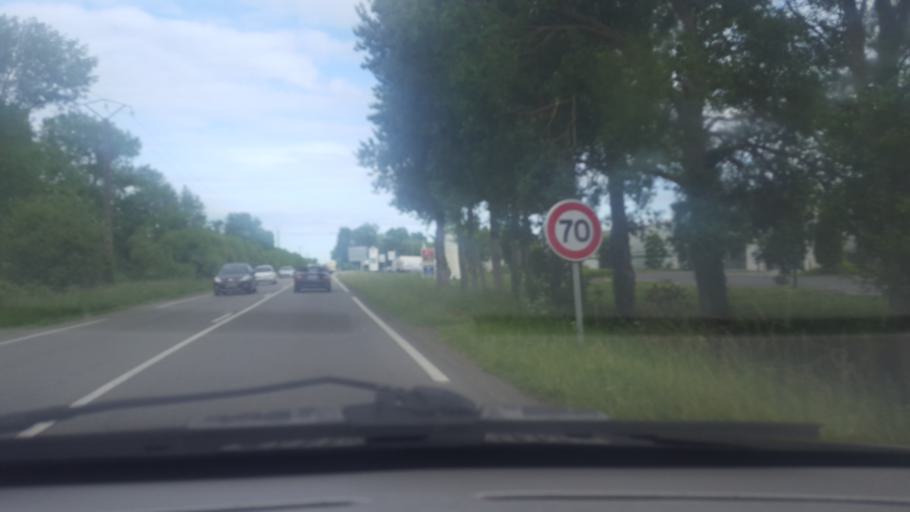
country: FR
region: Pays de la Loire
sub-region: Departement de la Loire-Atlantique
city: Machecoul
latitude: 46.9991
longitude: -1.8160
